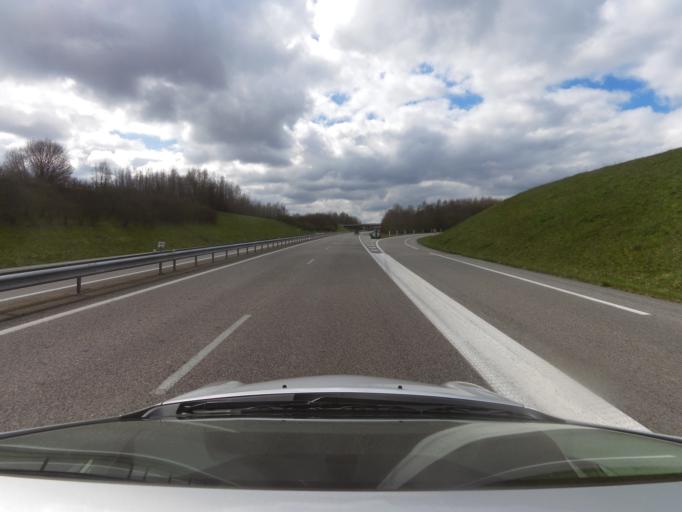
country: FR
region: Haute-Normandie
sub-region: Departement de la Seine-Maritime
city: Beuzeville-la-Grenier
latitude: 49.5836
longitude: 0.4419
